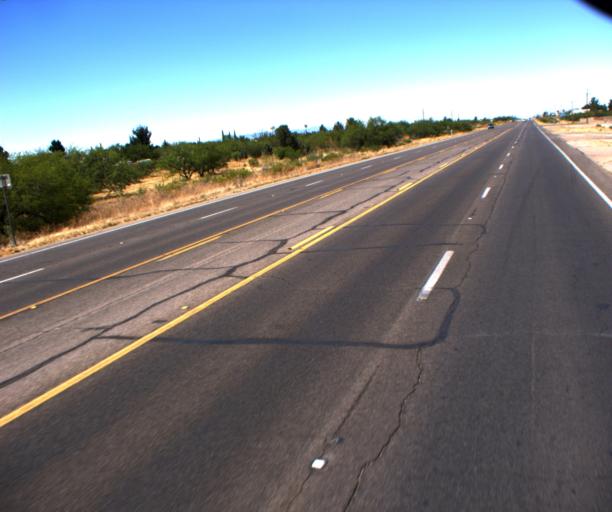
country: US
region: Arizona
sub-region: Cochise County
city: Sierra Vista Southeast
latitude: 31.4690
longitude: -110.2573
